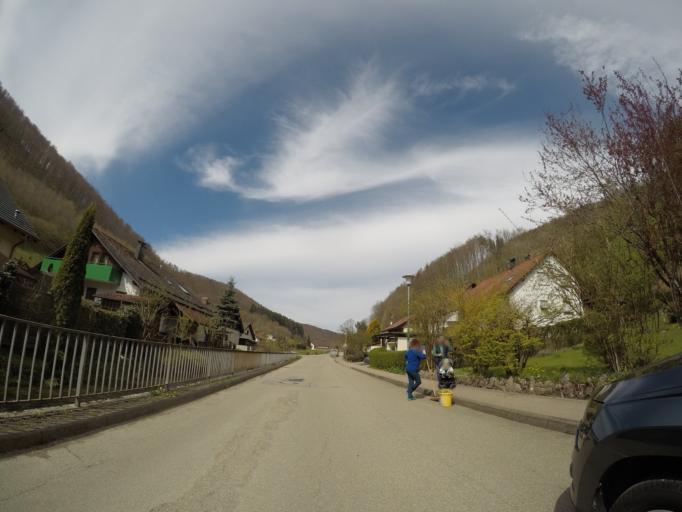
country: DE
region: Baden-Wuerttemberg
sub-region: Regierungsbezirk Stuttgart
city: Wiesensteig
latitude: 48.5623
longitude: 9.6152
